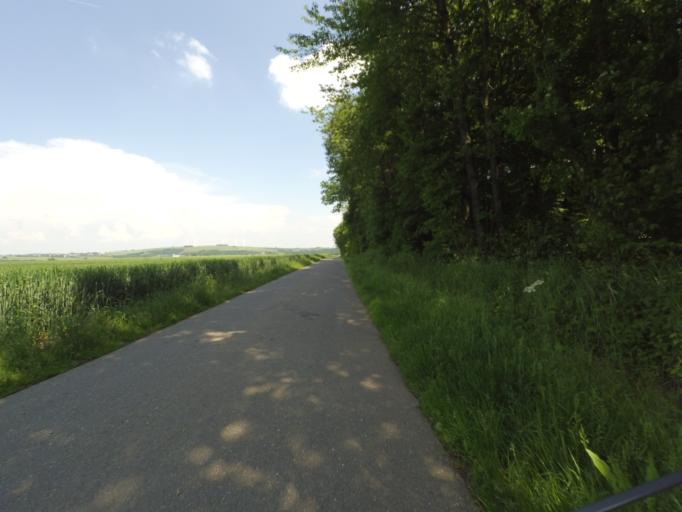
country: DE
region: Rheinland-Pfalz
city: Dunfus
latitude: 50.2189
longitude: 7.2199
